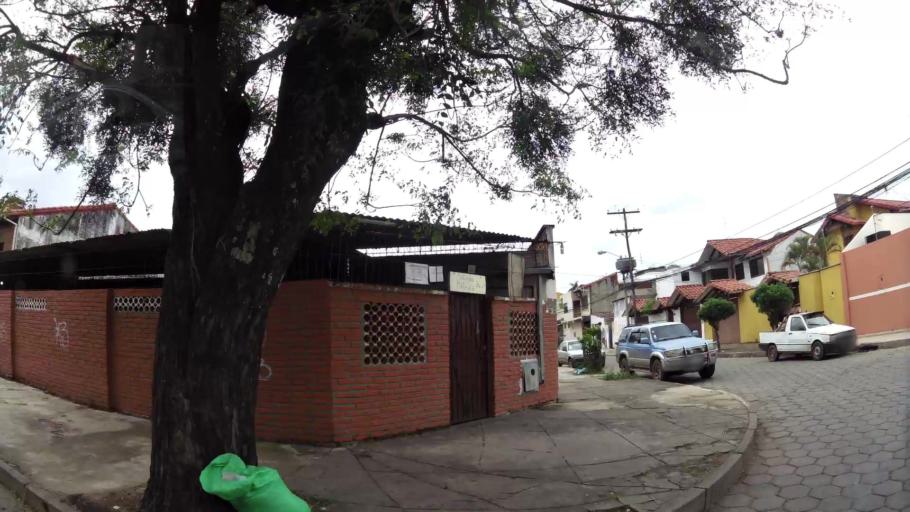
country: BO
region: Santa Cruz
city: Santa Cruz de la Sierra
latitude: -17.7723
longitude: -63.1705
